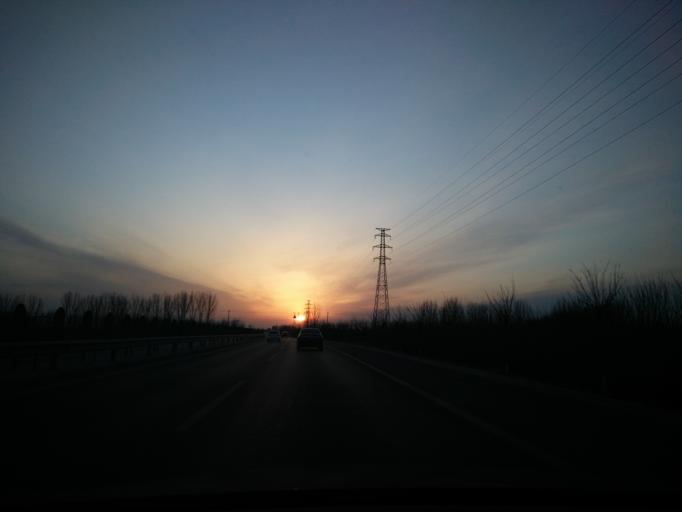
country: CN
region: Beijing
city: Qingyundian
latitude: 39.6909
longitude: 116.4679
